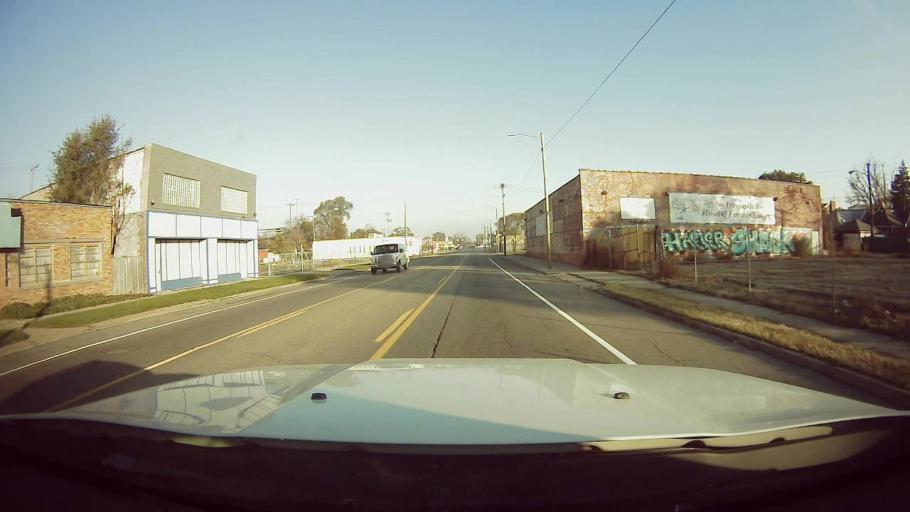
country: US
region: Michigan
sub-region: Oakland County
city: Oak Park
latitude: 42.4289
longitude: -83.1608
